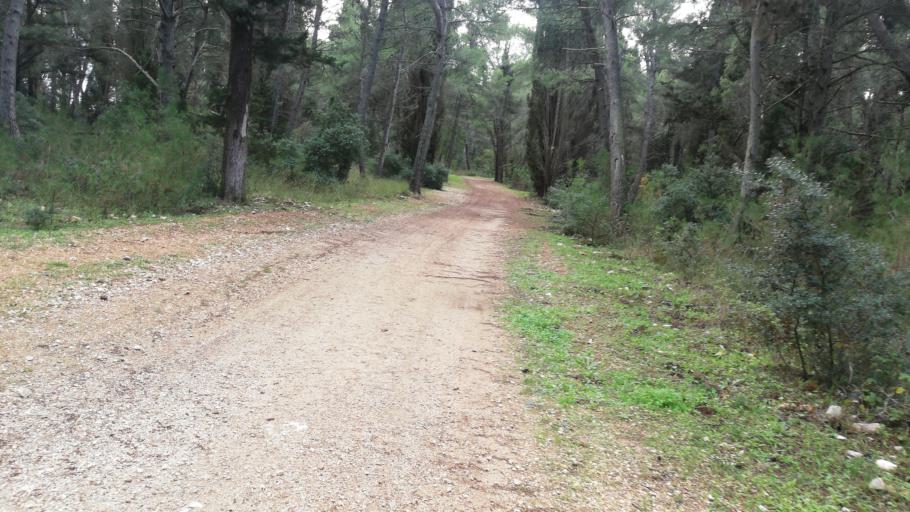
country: IT
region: Apulia
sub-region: Provincia di Bari
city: Cassano delle Murge
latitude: 40.8733
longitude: 16.7143
